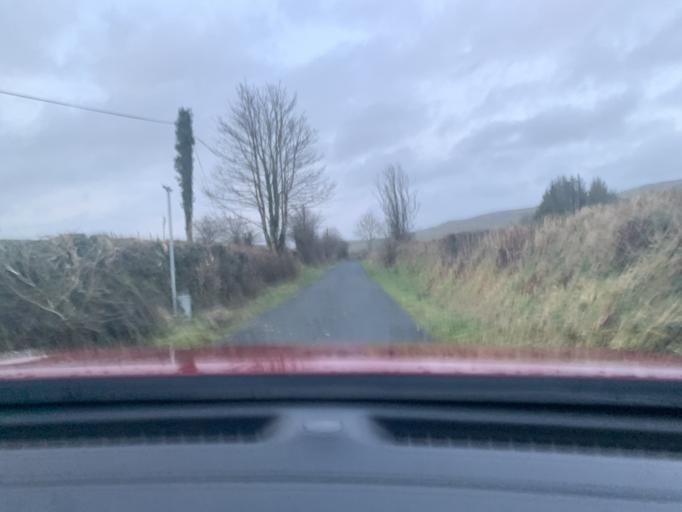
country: IE
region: Connaught
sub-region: Sligo
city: Ballymote
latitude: 54.0307
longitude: -8.4124
